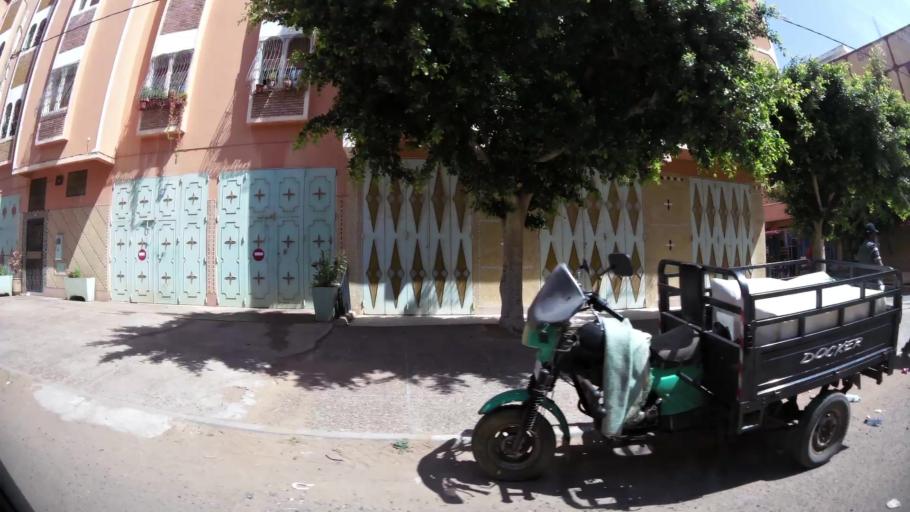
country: MA
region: Souss-Massa-Draa
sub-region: Inezgane-Ait Mellou
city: Inezgane
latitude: 30.3347
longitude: -9.5069
